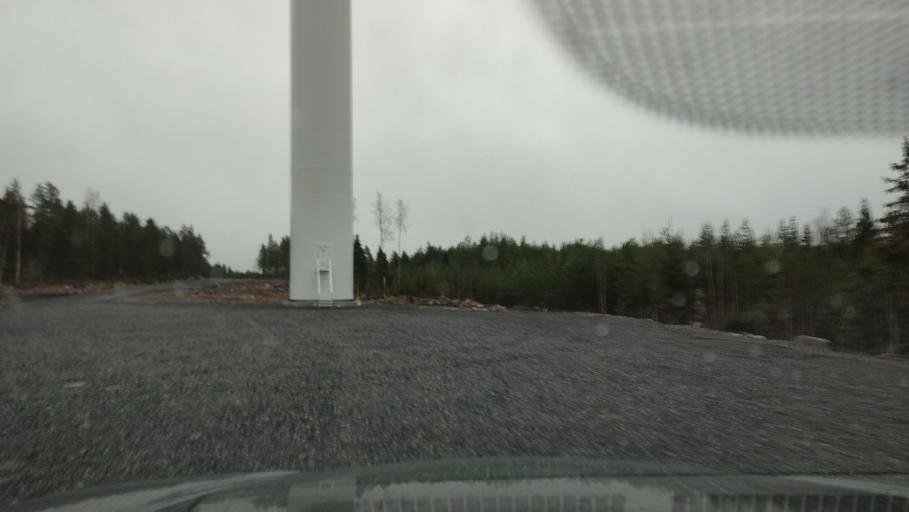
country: FI
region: Southern Ostrobothnia
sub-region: Suupohja
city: Karijoki
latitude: 62.1497
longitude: 21.6112
